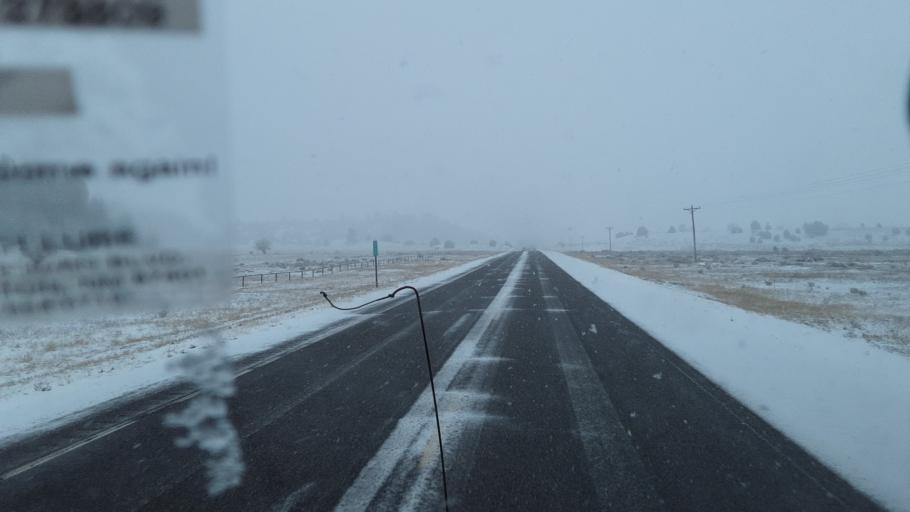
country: US
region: New Mexico
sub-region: Rio Arriba County
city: Chama
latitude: 36.8900
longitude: -106.7563
